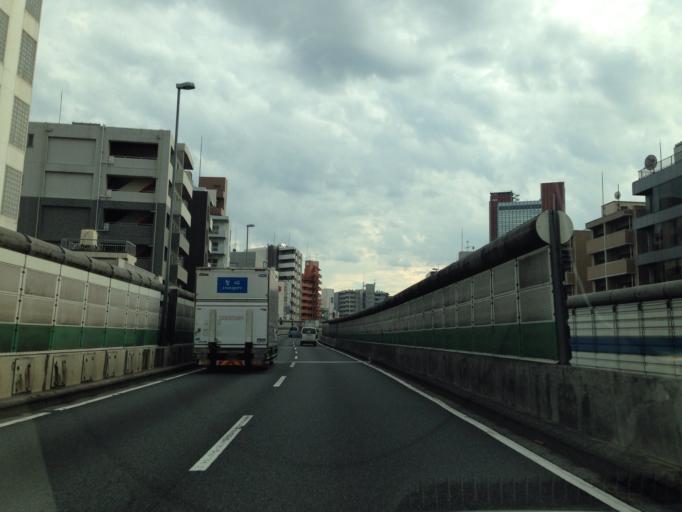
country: JP
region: Tokyo
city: Tokyo
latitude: 35.6451
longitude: 139.6742
